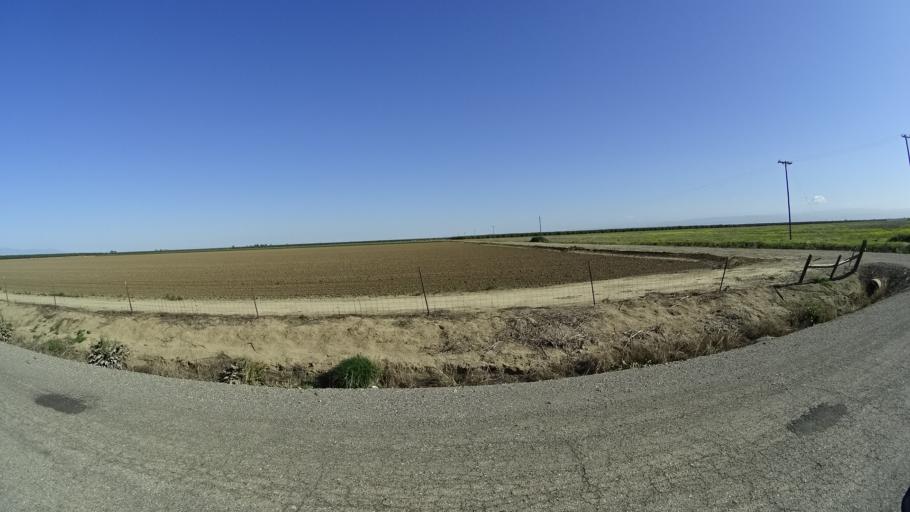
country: US
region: California
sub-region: Glenn County
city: Hamilton City
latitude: 39.6781
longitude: -122.0433
